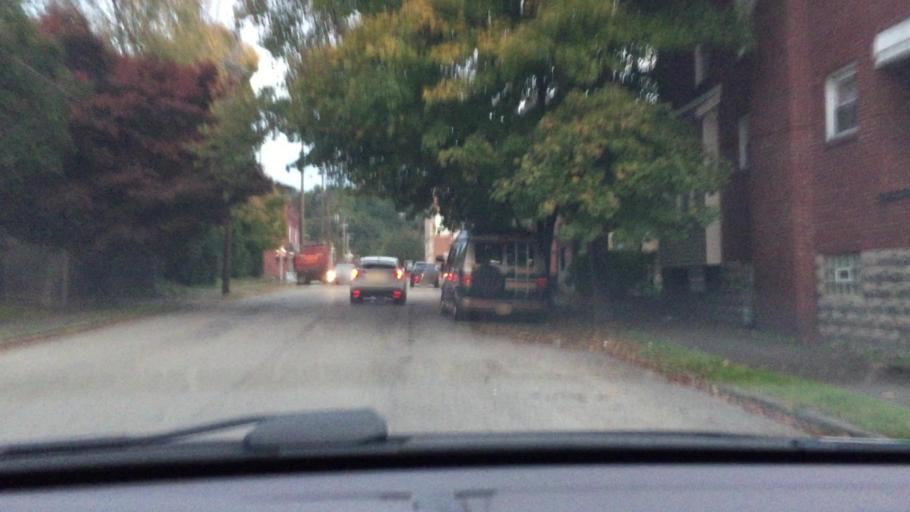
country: US
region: Pennsylvania
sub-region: Westmoreland County
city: Lower Burrell
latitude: 40.5568
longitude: -79.7630
